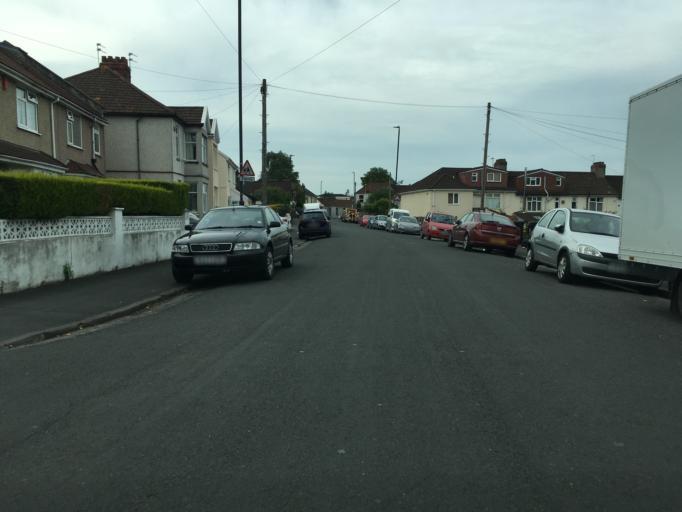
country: GB
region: England
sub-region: Bristol
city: Bristol
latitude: 51.4639
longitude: -2.5575
